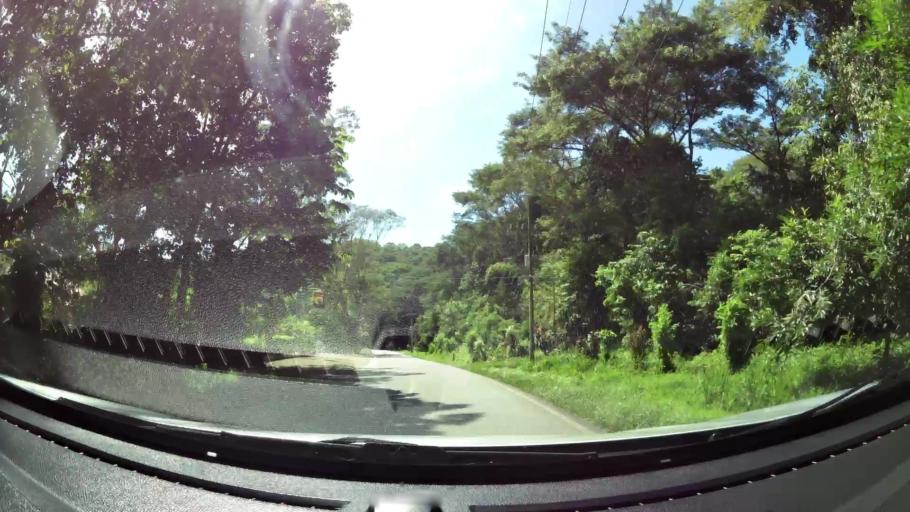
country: CR
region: San Jose
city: San Isidro
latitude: 9.2682
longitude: -83.8634
